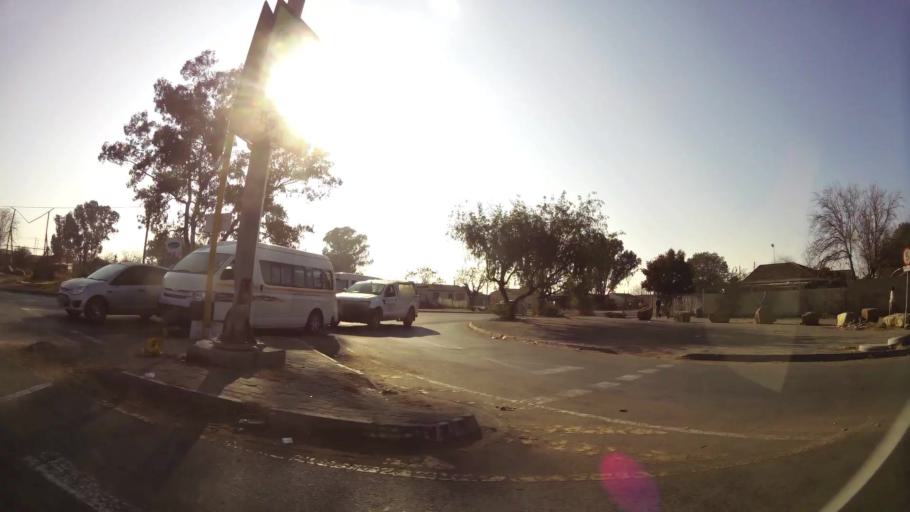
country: ZA
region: Orange Free State
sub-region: Mangaung Metropolitan Municipality
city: Bloemfontein
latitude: -29.1409
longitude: 26.2472
